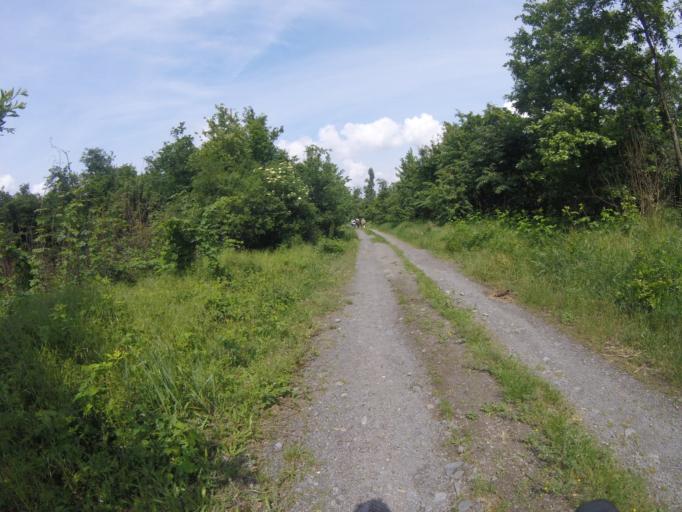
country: HU
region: Zala
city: Turje
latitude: 46.9118
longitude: 17.1818
